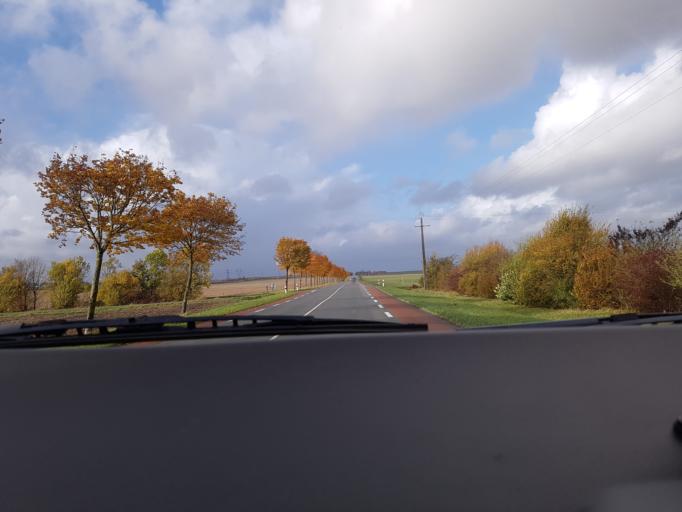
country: FR
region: Poitou-Charentes
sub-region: Departement de la Charente-Maritime
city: Les Gonds
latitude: 45.6579
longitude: -0.5908
